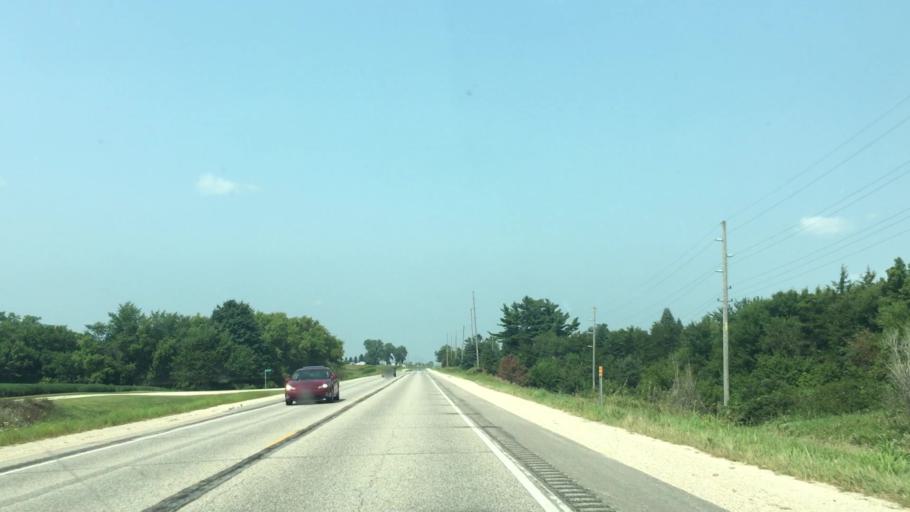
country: US
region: Iowa
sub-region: Fayette County
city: Fayette
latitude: 42.8750
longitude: -91.8105
